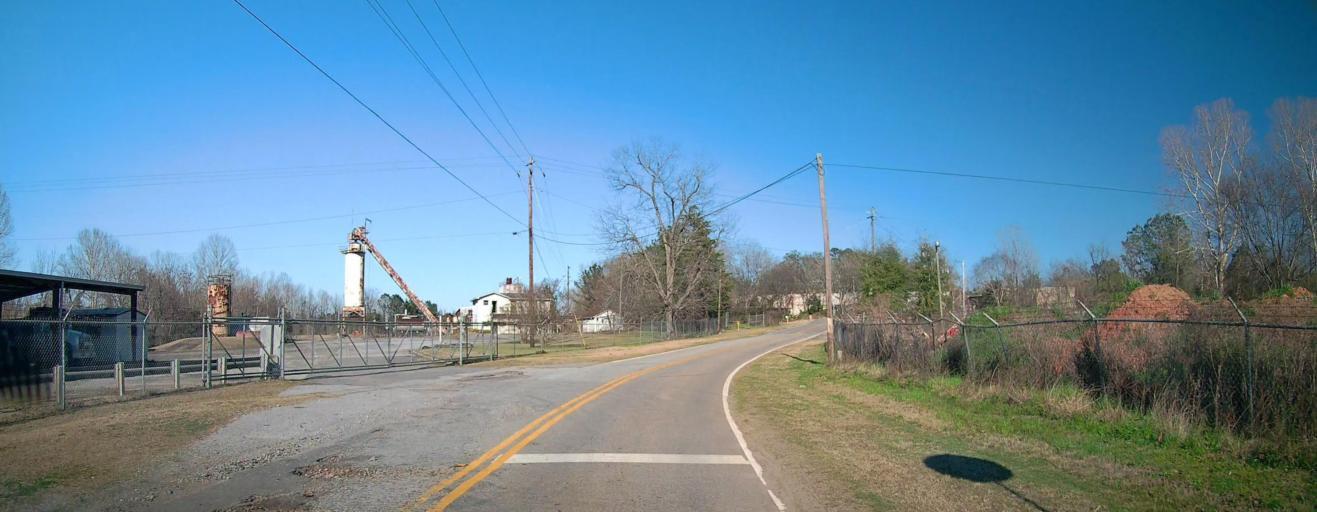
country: US
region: Georgia
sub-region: Sumter County
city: Americus
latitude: 32.0705
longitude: -84.2440
